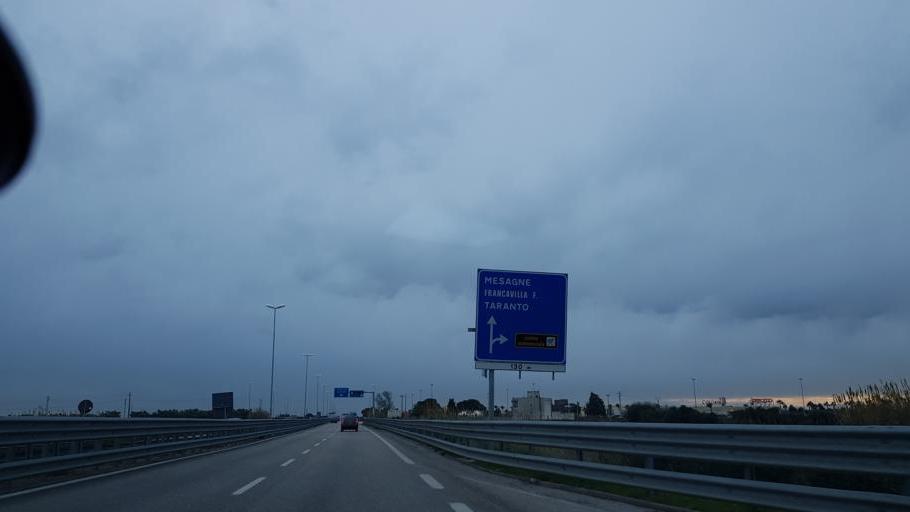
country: IT
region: Apulia
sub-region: Provincia di Brindisi
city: Brindisi
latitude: 40.6205
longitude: 17.9099
